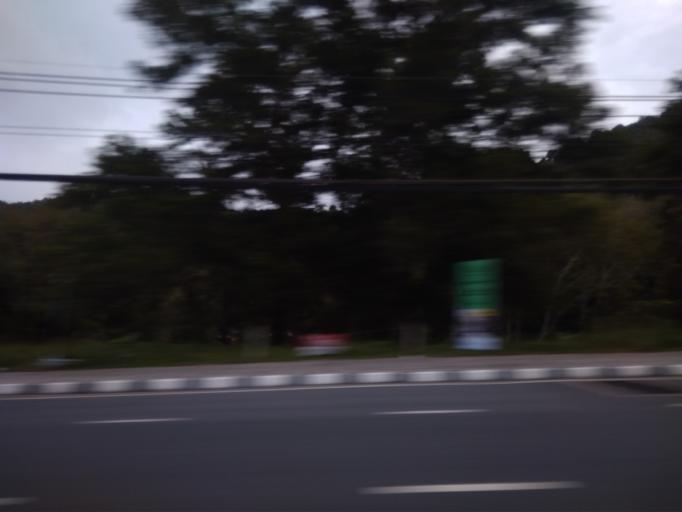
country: TH
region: Phuket
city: Wichit
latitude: 7.8980
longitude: 98.3685
